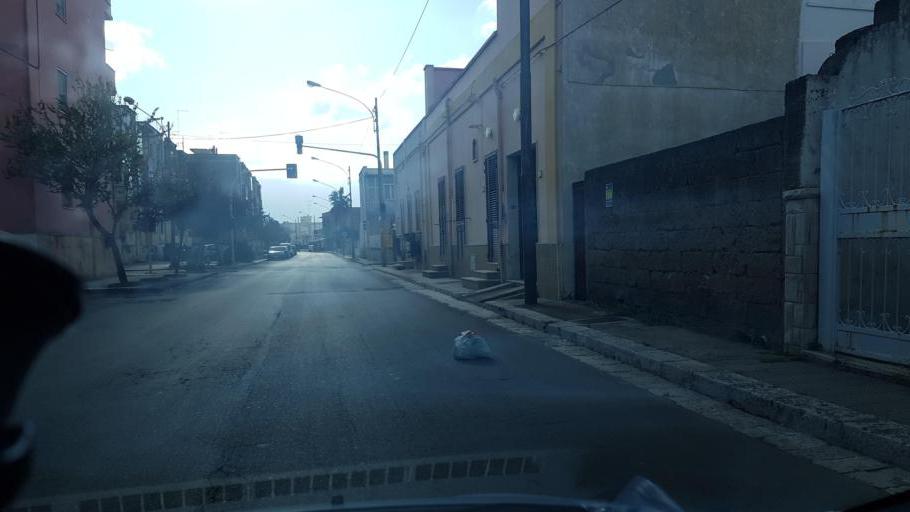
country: IT
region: Apulia
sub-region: Provincia di Lecce
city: Squinzano
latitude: 40.4383
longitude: 18.0347
